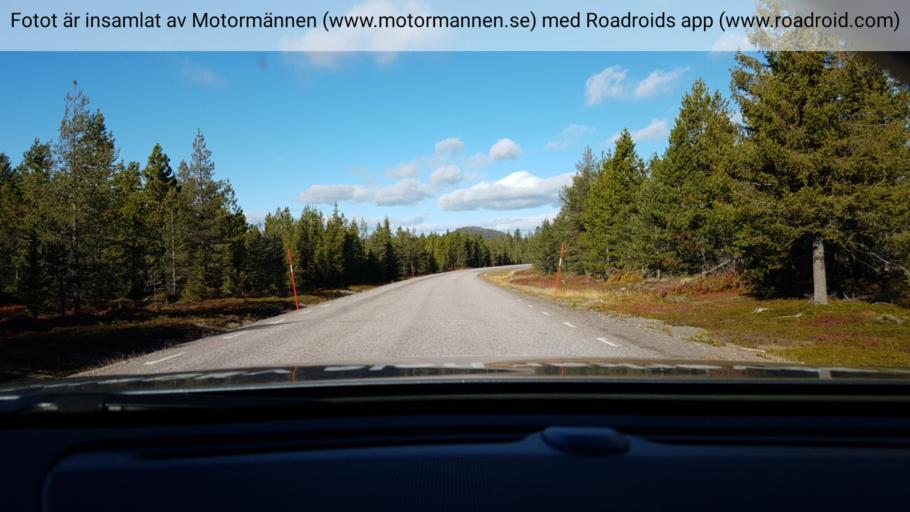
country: SE
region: Norrbotten
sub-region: Arjeplogs Kommun
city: Arjeplog
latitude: 65.8456
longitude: 18.4085
